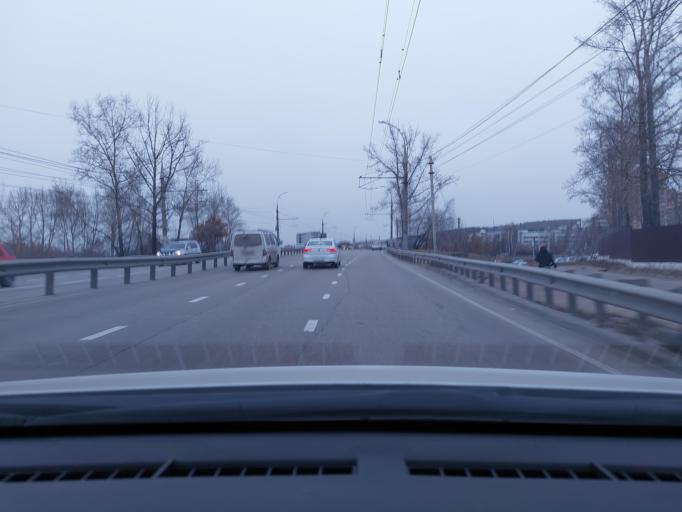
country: RU
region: Irkutsk
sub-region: Irkutskiy Rayon
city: Irkutsk
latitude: 52.2565
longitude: 104.2629
